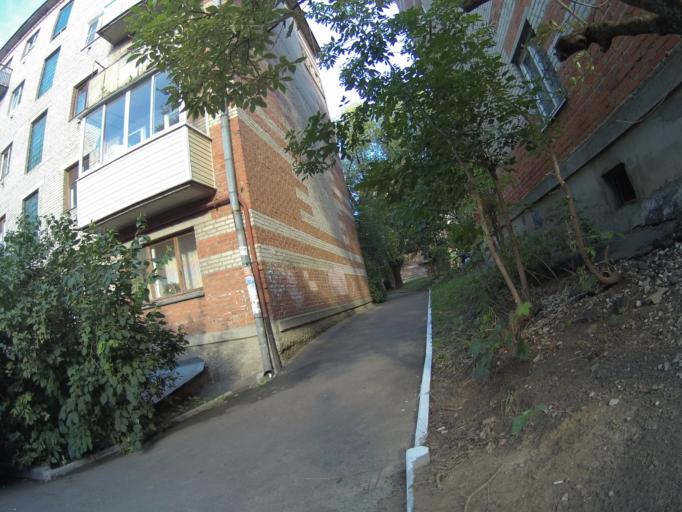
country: RU
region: Vladimir
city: Vladimir
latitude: 56.1516
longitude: 40.3718
